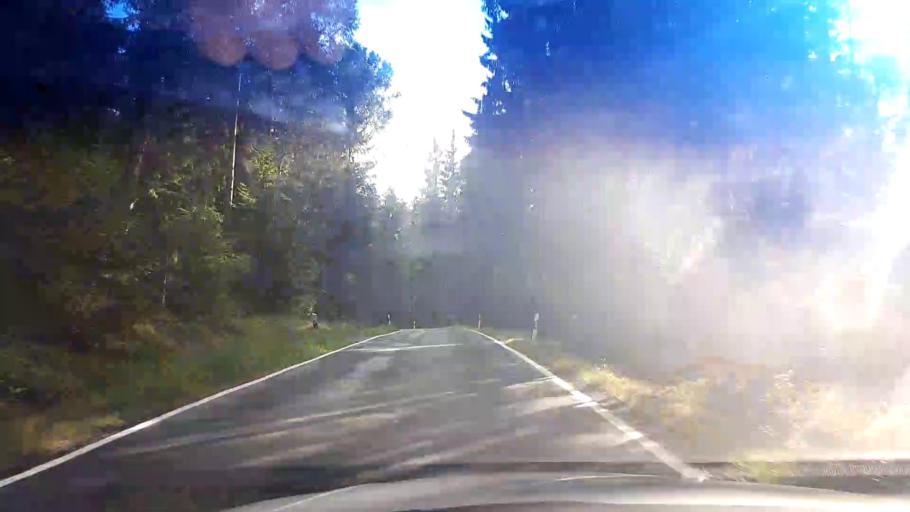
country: DE
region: Bavaria
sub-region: Upper Palatinate
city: Neualbenreuth
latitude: 49.9510
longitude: 12.4189
